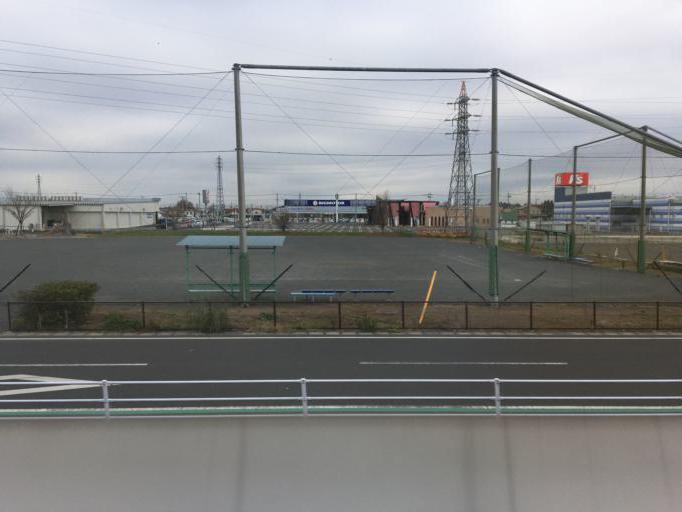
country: JP
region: Tochigi
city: Tochigi
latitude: 36.3505
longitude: 139.7058
